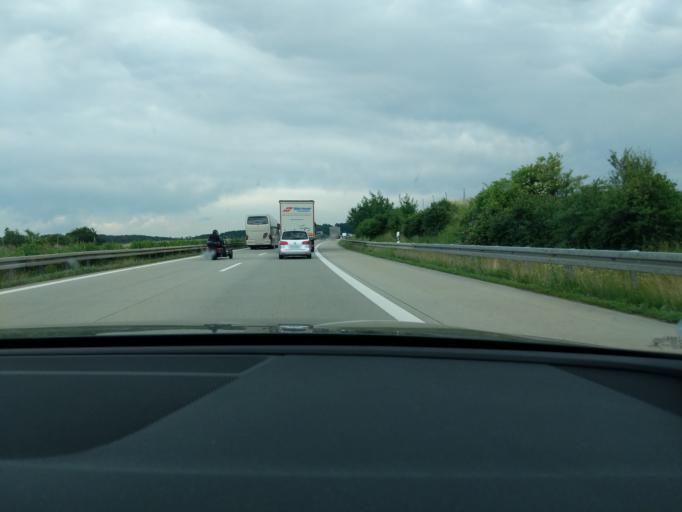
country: DE
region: Saxony
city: Wildenfels
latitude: 50.6880
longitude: 12.6107
